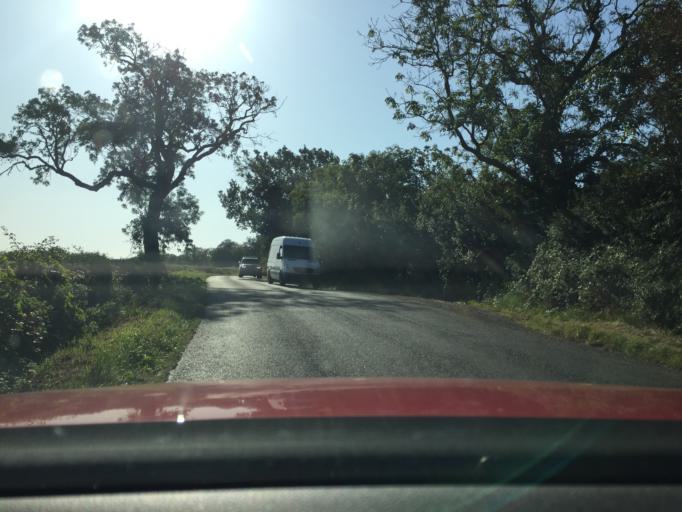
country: GB
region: England
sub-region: Leicestershire
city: Houghton on the Hill
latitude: 52.6564
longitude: -1.0152
